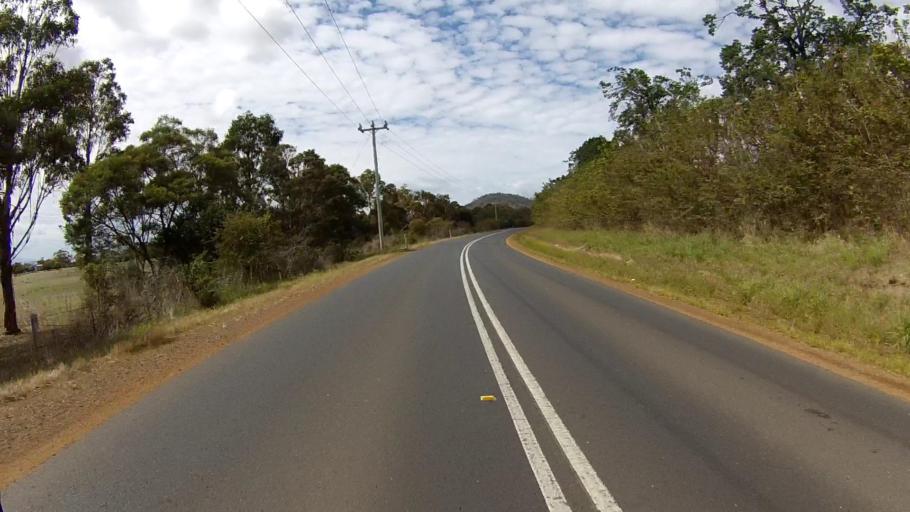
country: AU
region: Tasmania
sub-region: Clarence
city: Cambridge
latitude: -42.7995
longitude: 147.4221
